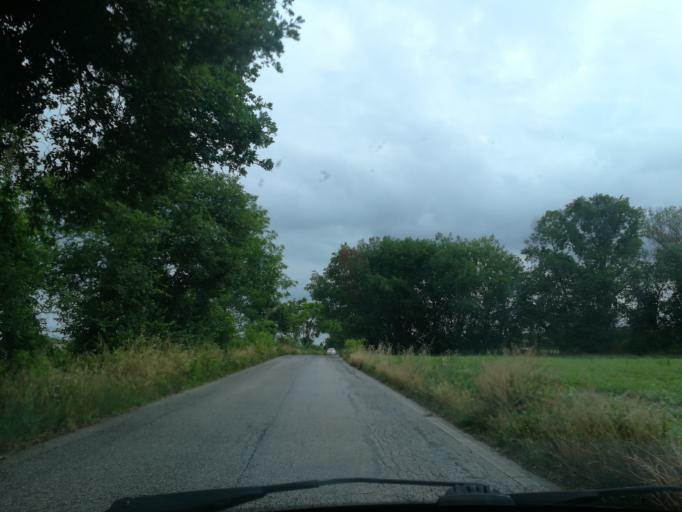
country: IT
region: The Marches
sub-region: Provincia di Macerata
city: Petriolo
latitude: 43.2371
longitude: 13.4694
